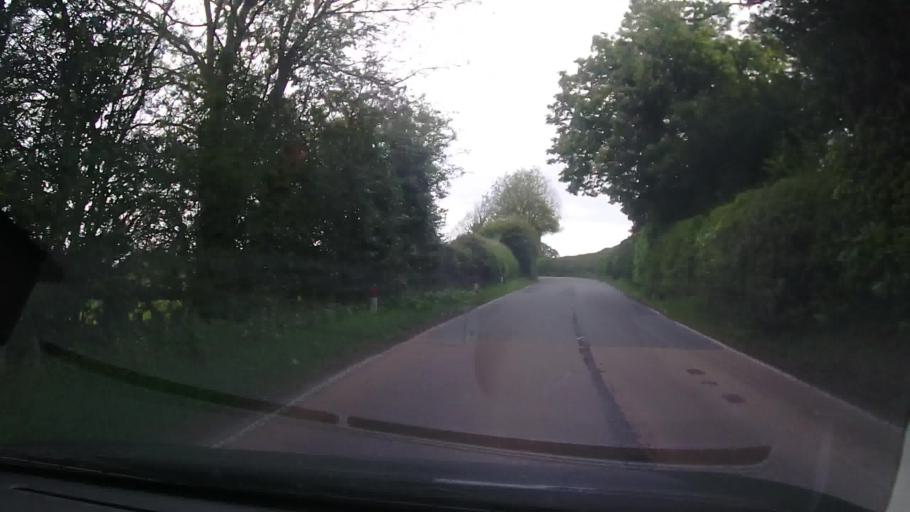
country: GB
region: Wales
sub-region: Wrexham
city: Overton
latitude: 52.9644
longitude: -2.9199
